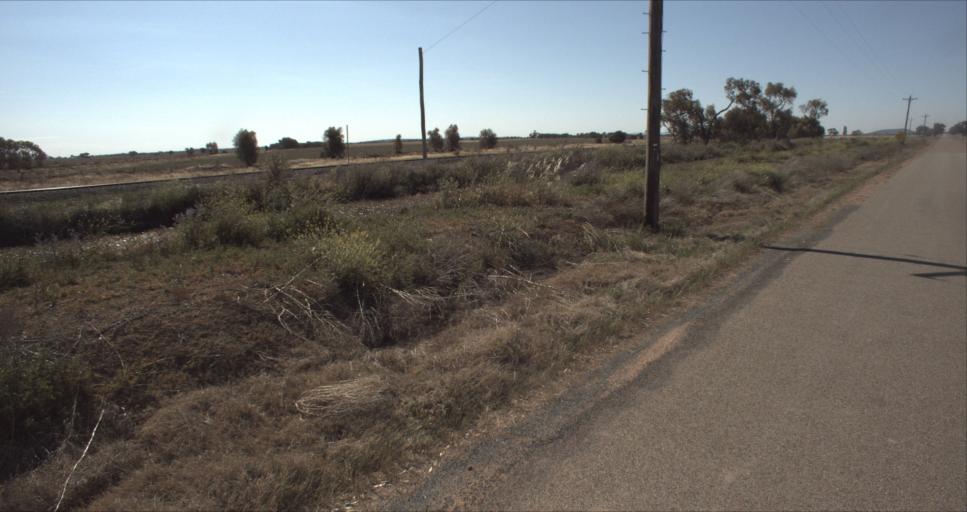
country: AU
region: New South Wales
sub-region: Leeton
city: Leeton
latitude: -34.4775
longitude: 146.3680
